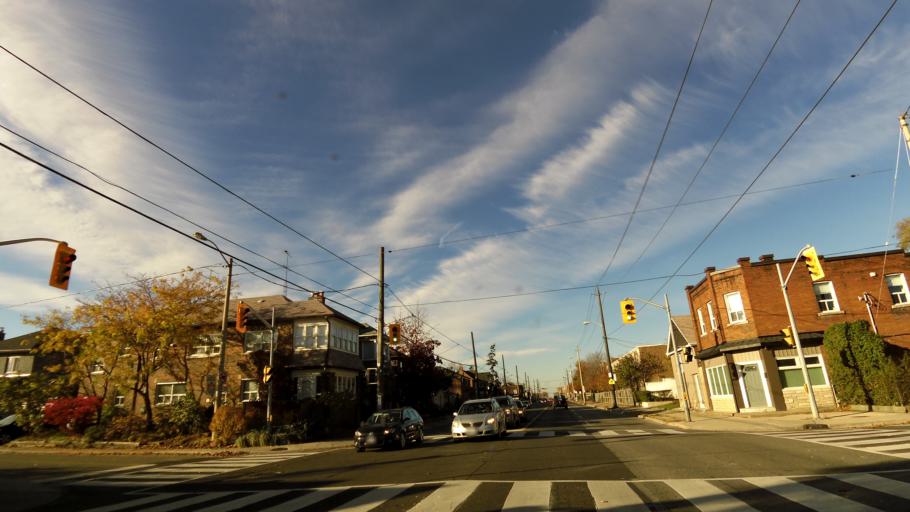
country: CA
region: Ontario
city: Etobicoke
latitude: 43.6618
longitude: -79.4896
